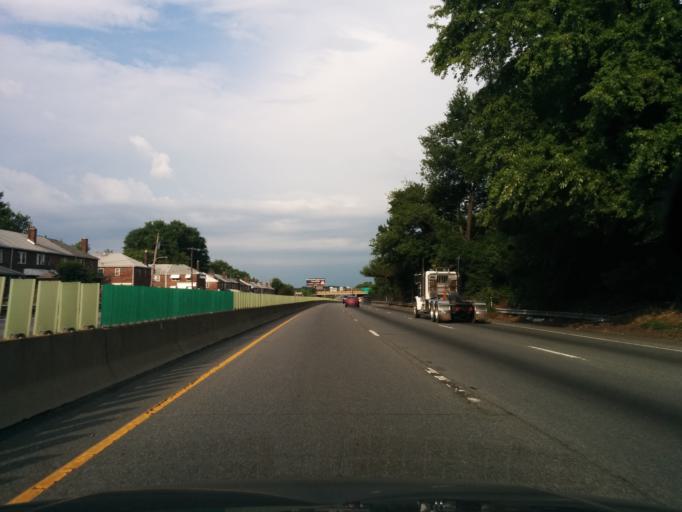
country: US
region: Pennsylvania
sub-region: Delaware County
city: Upland
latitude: 39.8430
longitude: -75.3977
